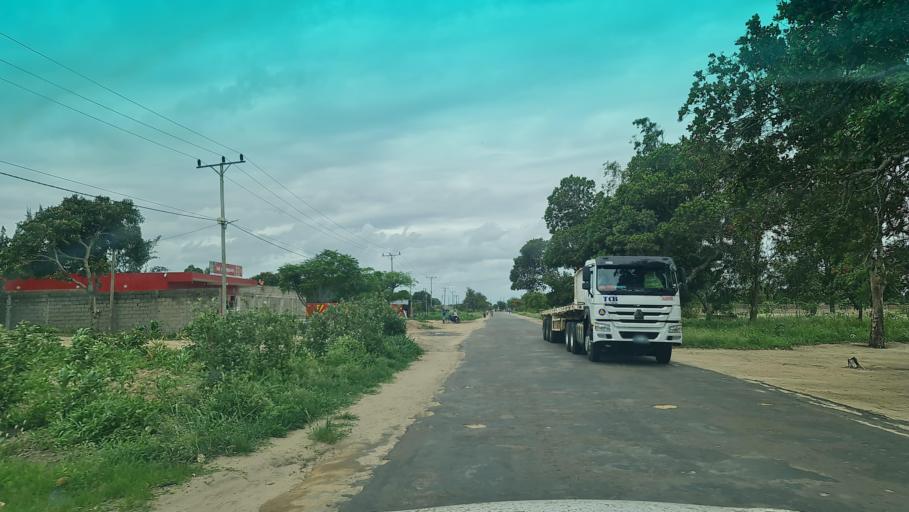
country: MZ
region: Maputo
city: Manhica
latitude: -25.4137
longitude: 32.7725
